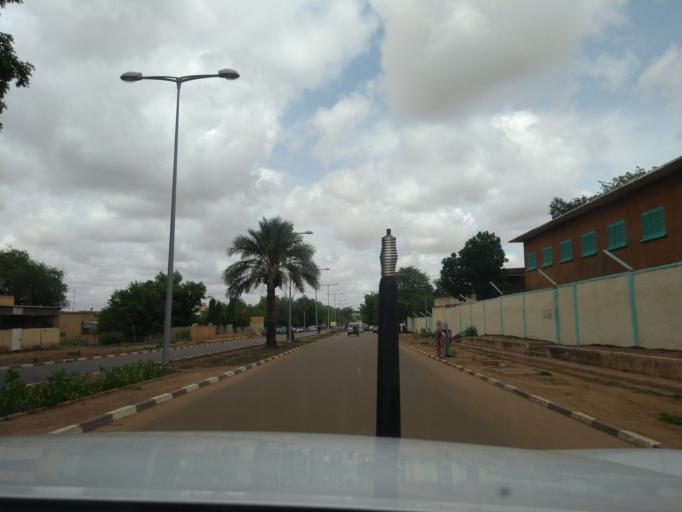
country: NE
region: Niamey
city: Niamey
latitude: 13.5134
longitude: 2.1028
